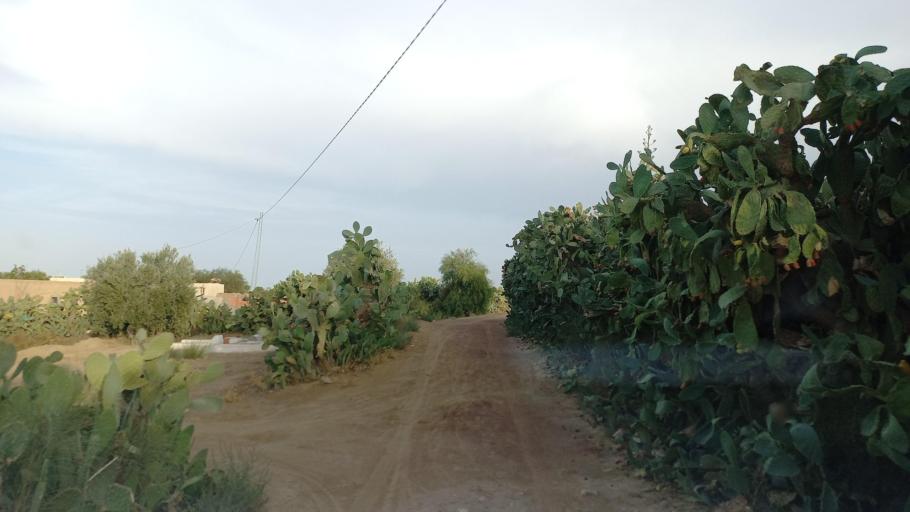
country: TN
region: Al Qasrayn
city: Kasserine
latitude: 35.2173
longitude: 9.0549
